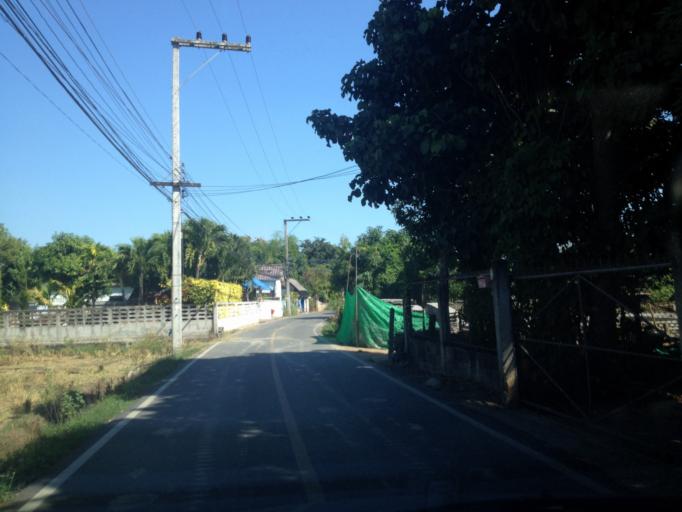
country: TH
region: Chiang Mai
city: Hang Dong
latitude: 18.6846
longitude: 98.9123
